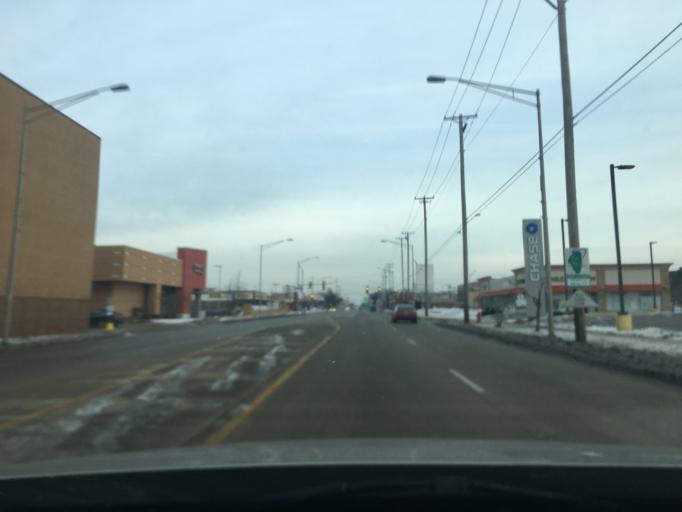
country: US
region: Illinois
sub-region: Cook County
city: Harwood Heights
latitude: 41.9570
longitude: -87.8072
